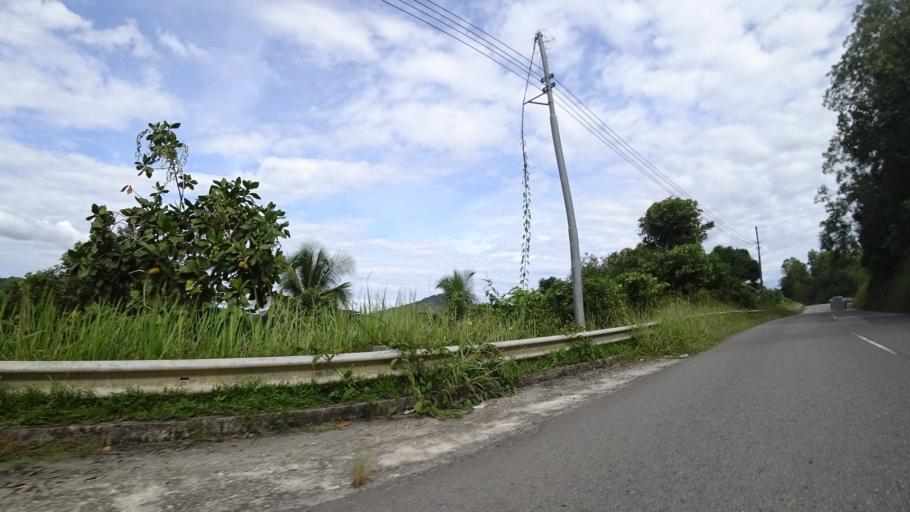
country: BN
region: Brunei and Muara
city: Bandar Seri Begawan
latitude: 4.8610
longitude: 114.9500
